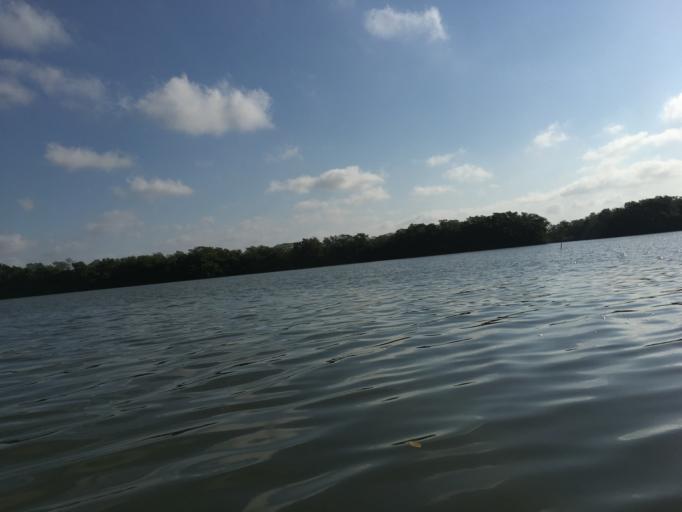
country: CO
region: Bolivar
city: Cartagena
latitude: 10.4877
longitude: -75.4815
